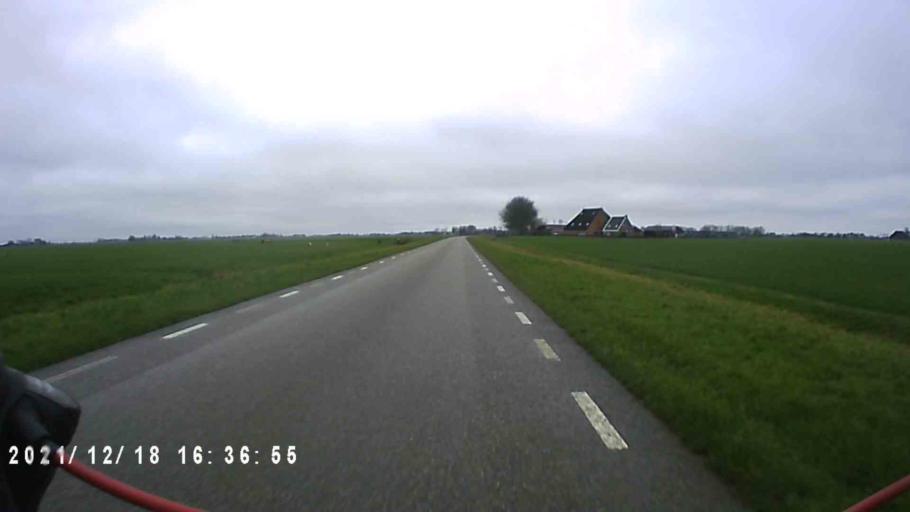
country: NL
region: Friesland
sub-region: Gemeente Dongeradeel
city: Dokkum
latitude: 53.3576
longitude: 6.0185
